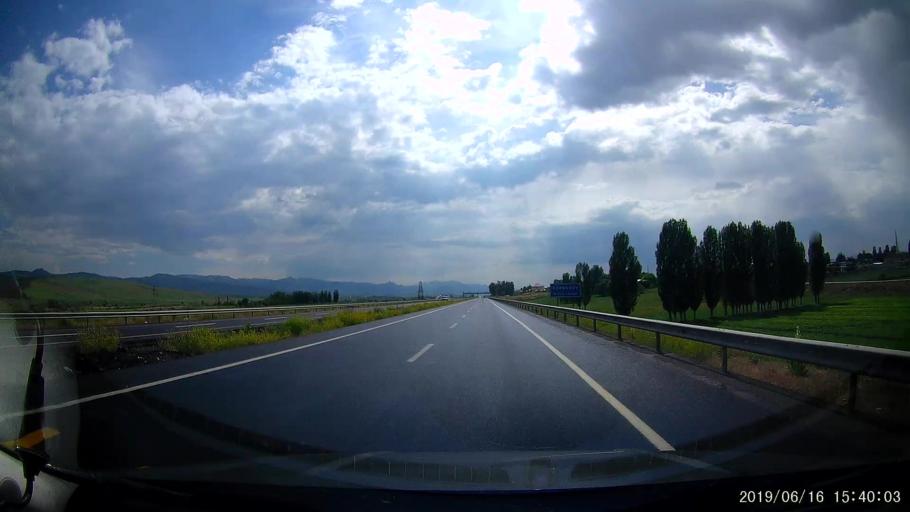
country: TR
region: Erzurum
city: Koprukoy
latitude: 39.9690
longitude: 41.8805
